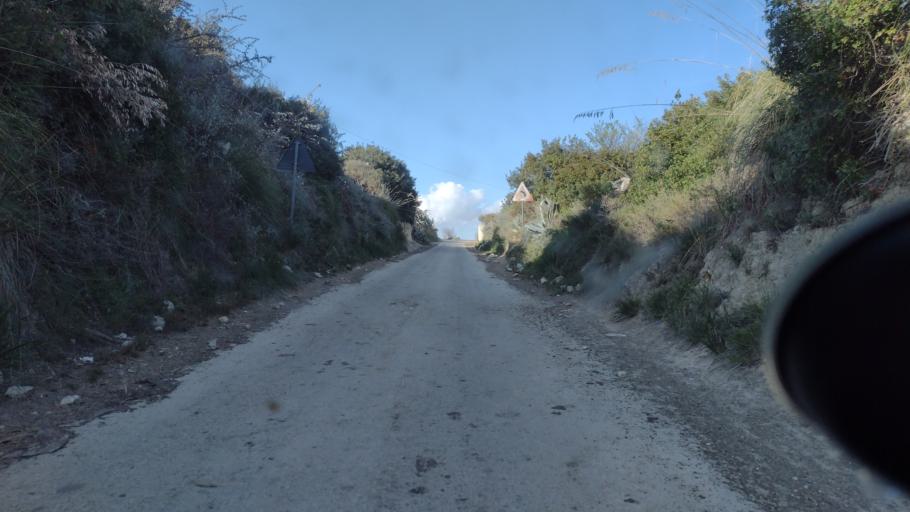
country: IT
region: Sicily
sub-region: Provincia di Siracusa
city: Noto
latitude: 36.8568
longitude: 15.0238
